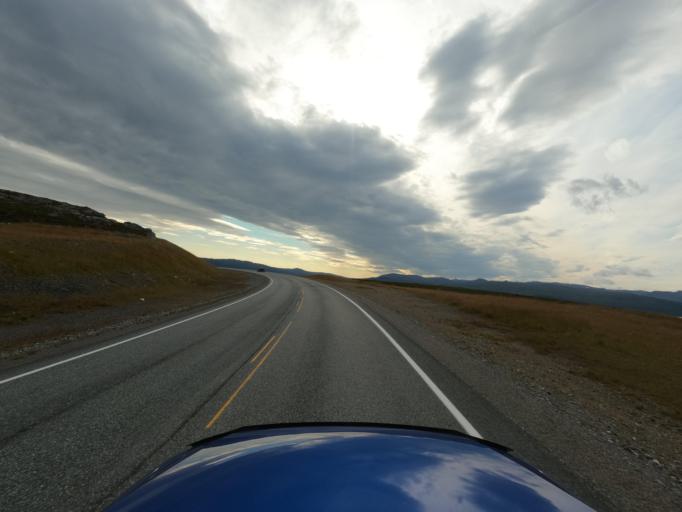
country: NO
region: Finnmark Fylke
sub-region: Hammerfest
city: Rypefjord
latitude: 70.5265
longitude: 23.7404
